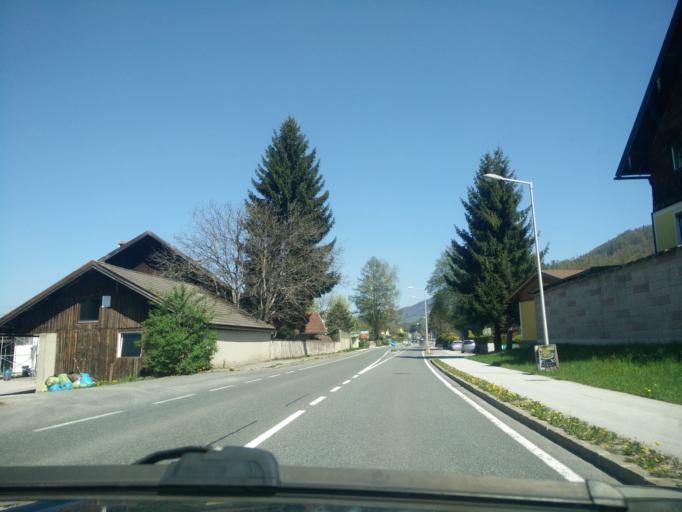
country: AT
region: Salzburg
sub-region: Politischer Bezirk Salzburg-Umgebung
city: Elsbethen
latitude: 47.7453
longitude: 13.0851
